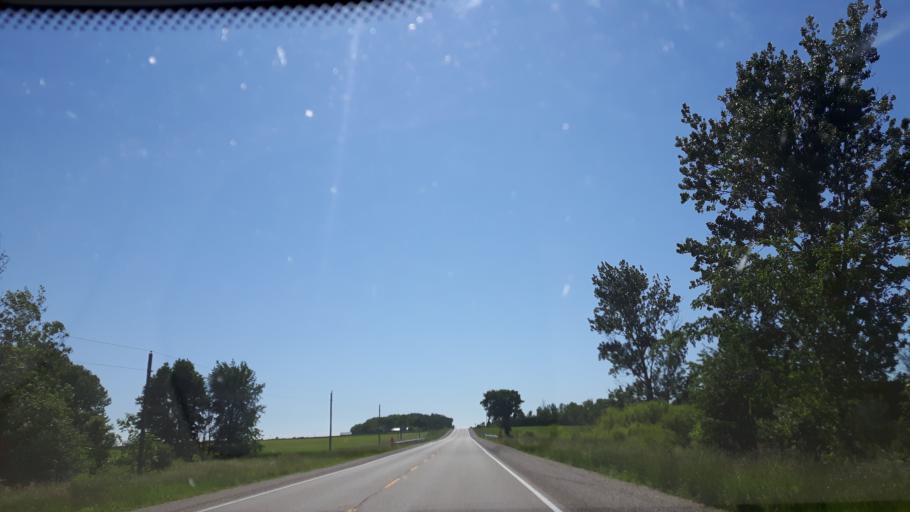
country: CA
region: Ontario
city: Bluewater
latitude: 43.4287
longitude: -81.5536
